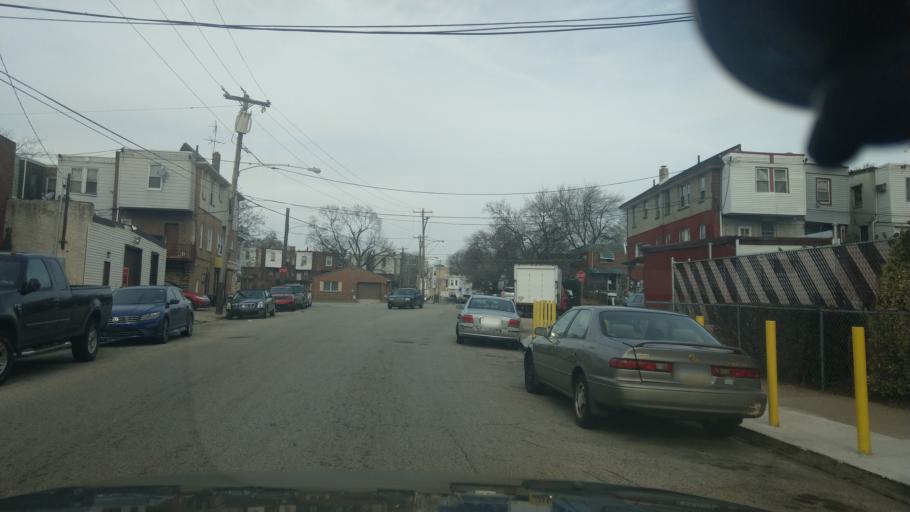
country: US
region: Pennsylvania
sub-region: Montgomery County
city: Wyncote
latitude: 40.0481
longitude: -75.1535
